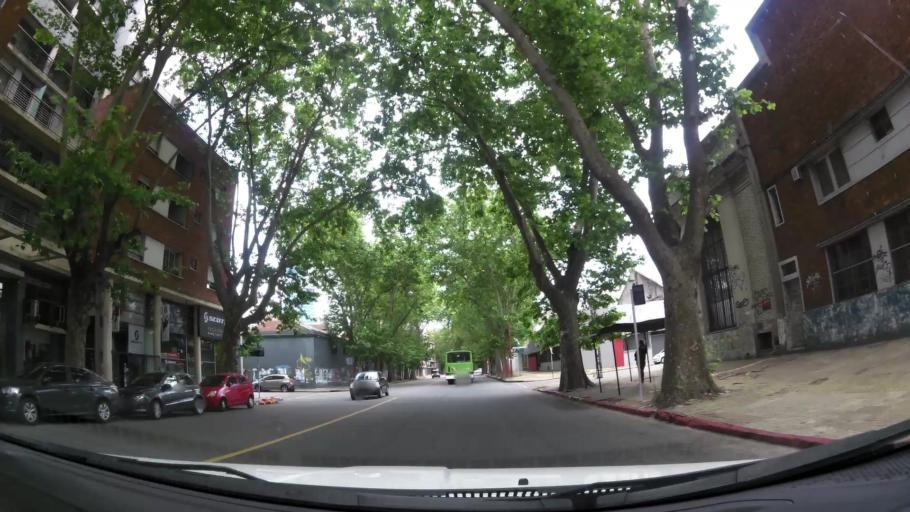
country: UY
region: Montevideo
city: Montevideo
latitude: -34.8962
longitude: -56.1924
